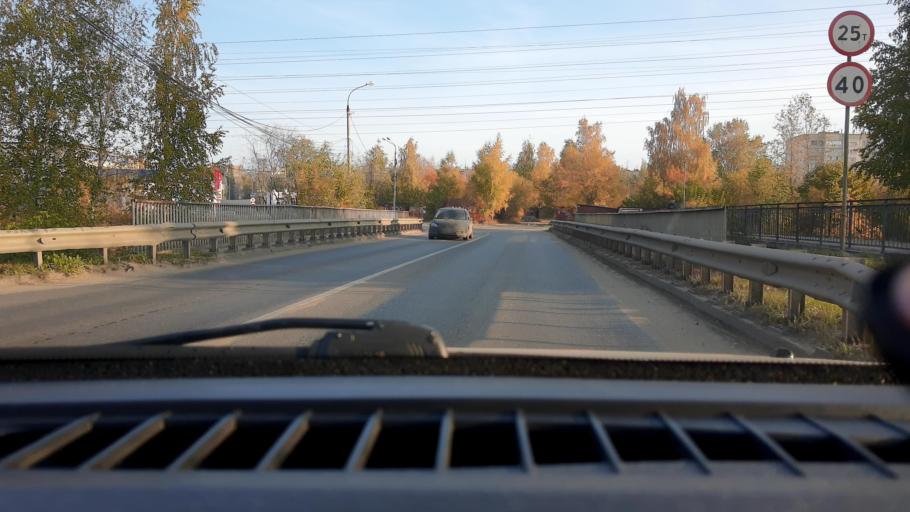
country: RU
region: Nizjnij Novgorod
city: Gorbatovka
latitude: 56.3564
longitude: 43.8057
